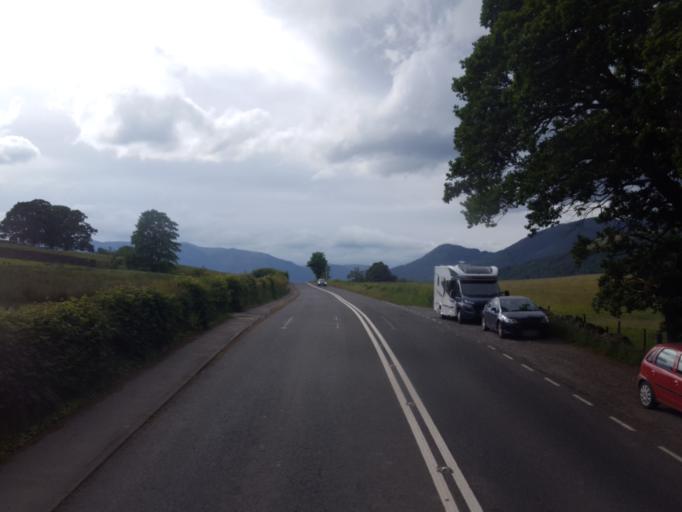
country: GB
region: England
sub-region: Cumbria
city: Keswick
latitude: 54.5947
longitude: -3.1040
